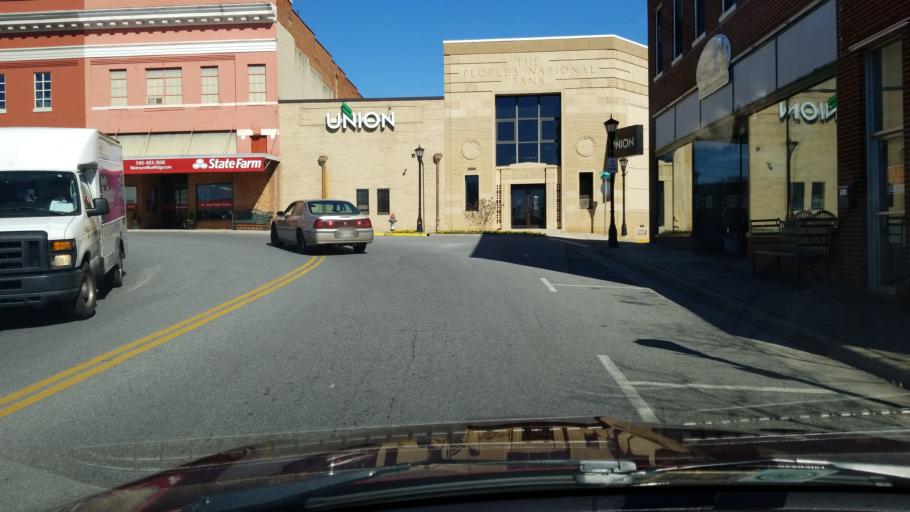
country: US
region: Virginia
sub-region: Franklin County
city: Rocky Mount
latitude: 36.9975
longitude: -79.8921
